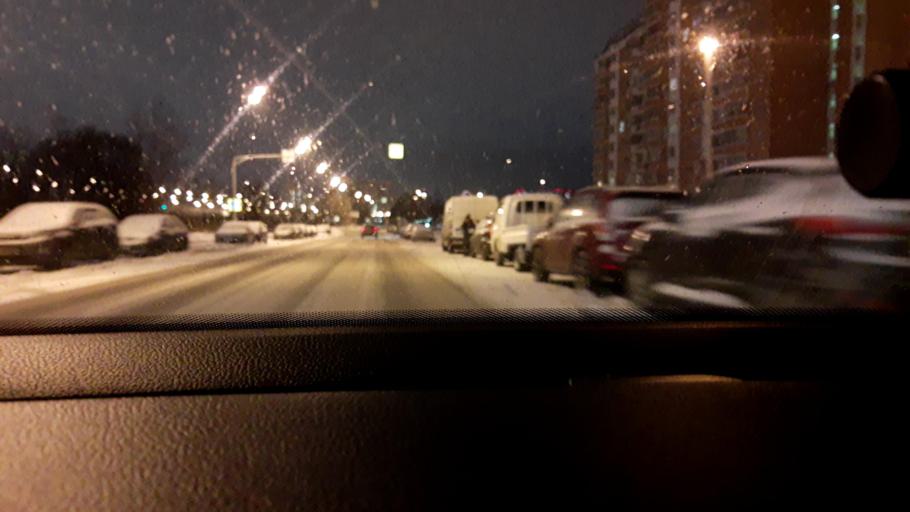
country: RU
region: Moscow
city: Vagonoremont
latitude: 55.9136
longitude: 37.5469
